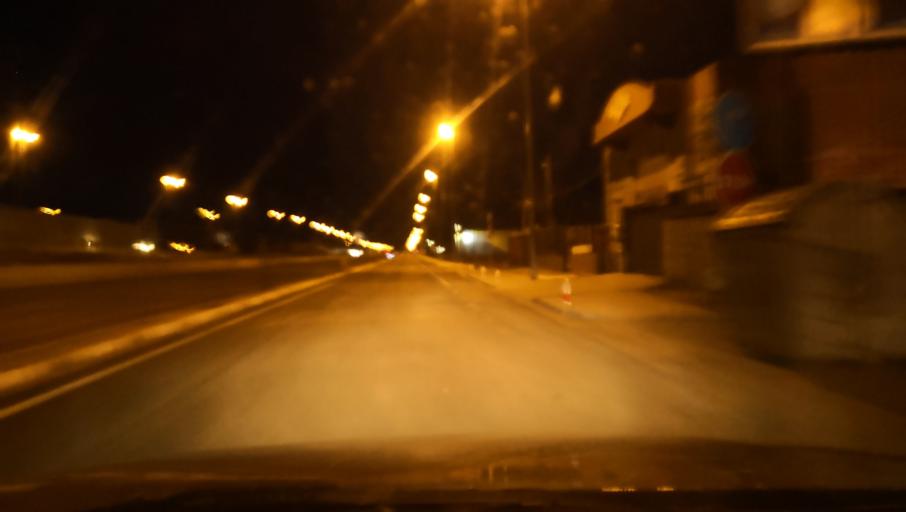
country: ES
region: Castille and Leon
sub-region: Provincia de Zamora
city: Zamora
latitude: 41.5213
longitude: -5.7556
